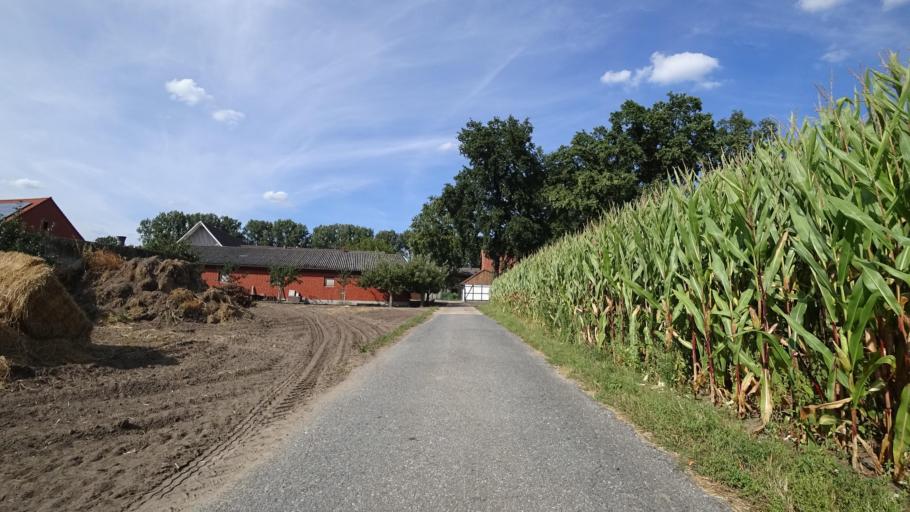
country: DE
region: North Rhine-Westphalia
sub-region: Regierungsbezirk Detmold
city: Guetersloh
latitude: 51.8945
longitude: 8.4006
